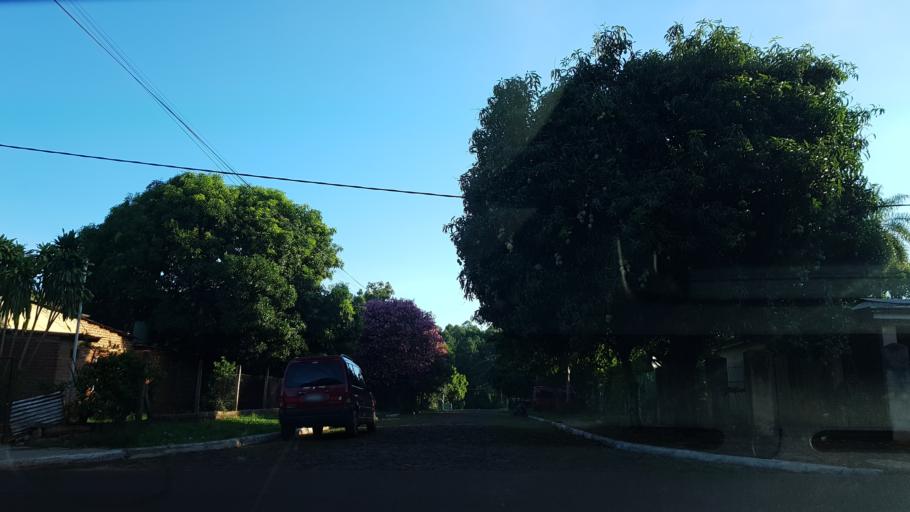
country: AR
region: Misiones
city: Puerto Libertad
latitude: -25.9229
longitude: -54.5833
